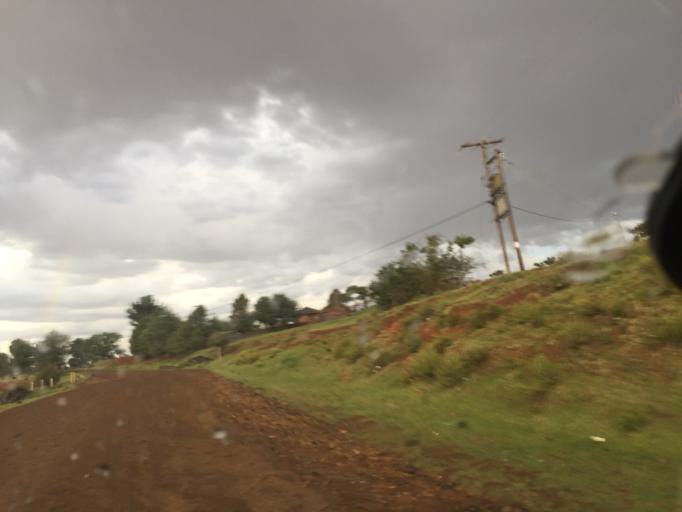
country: LS
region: Leribe
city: Leribe
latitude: -29.1574
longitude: 28.0346
